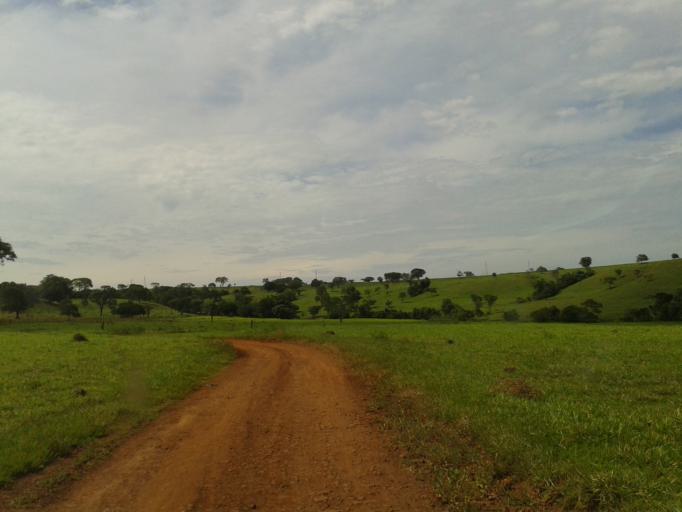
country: BR
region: Minas Gerais
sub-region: Centralina
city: Centralina
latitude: -18.6976
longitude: -49.2083
